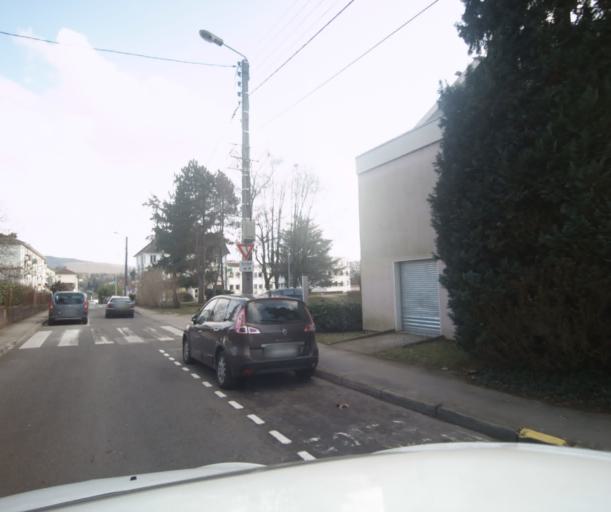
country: FR
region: Franche-Comte
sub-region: Departement du Doubs
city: Besancon
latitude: 47.2600
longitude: 6.0434
